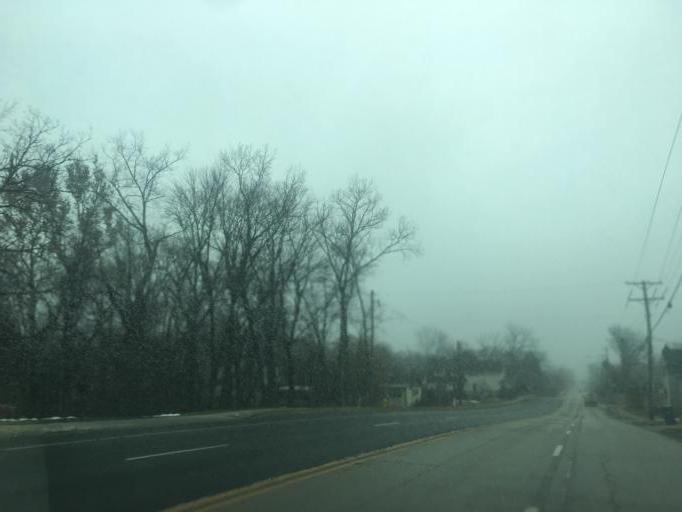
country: US
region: Illinois
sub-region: DuPage County
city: Downers Grove
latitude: 41.7876
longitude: -88.0088
